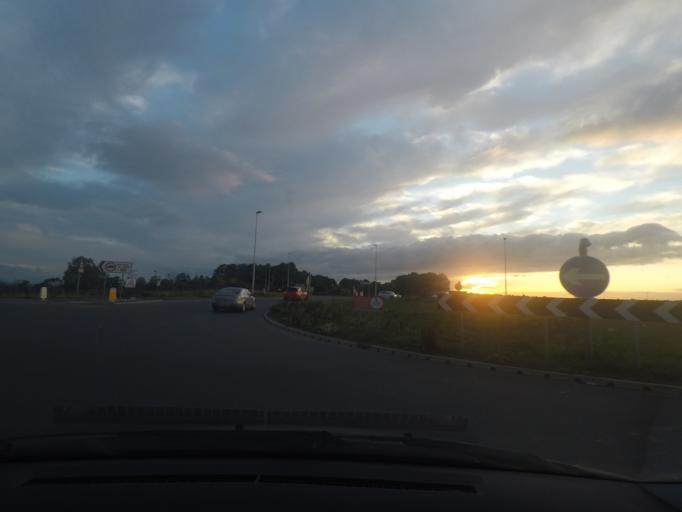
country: GB
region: England
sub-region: North Lincolnshire
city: Barnetby le Wold
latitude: 53.5824
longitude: -0.4108
